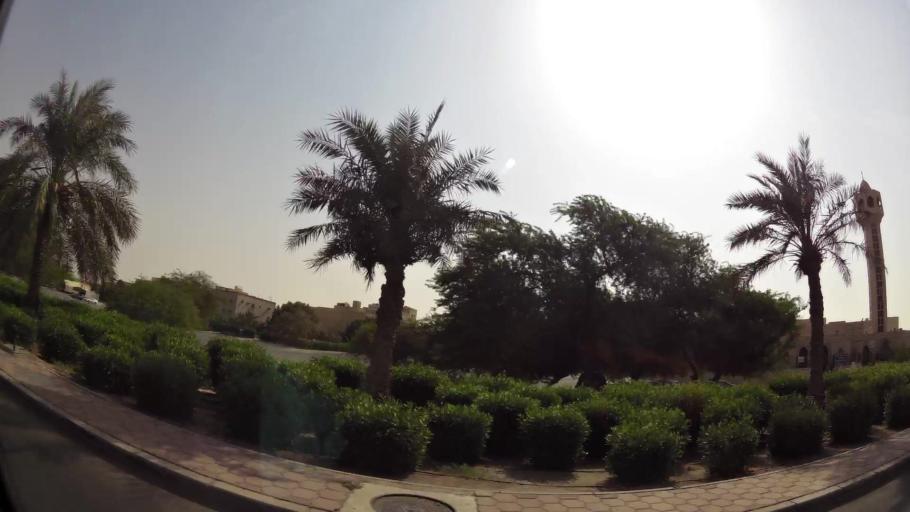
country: KW
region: Muhafazat al Jahra'
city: Al Jahra'
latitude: 29.3369
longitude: 47.6586
